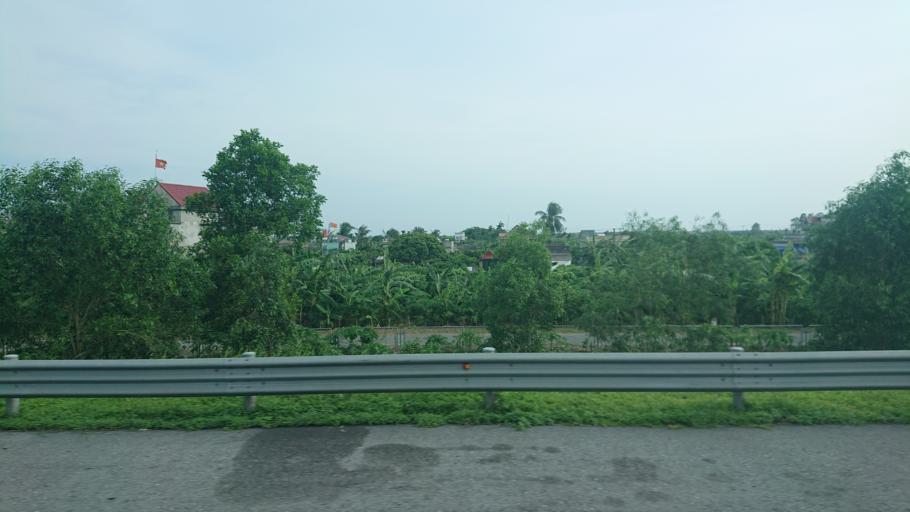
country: VN
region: Hai Phong
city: An Lao
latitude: 20.8124
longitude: 106.5007
